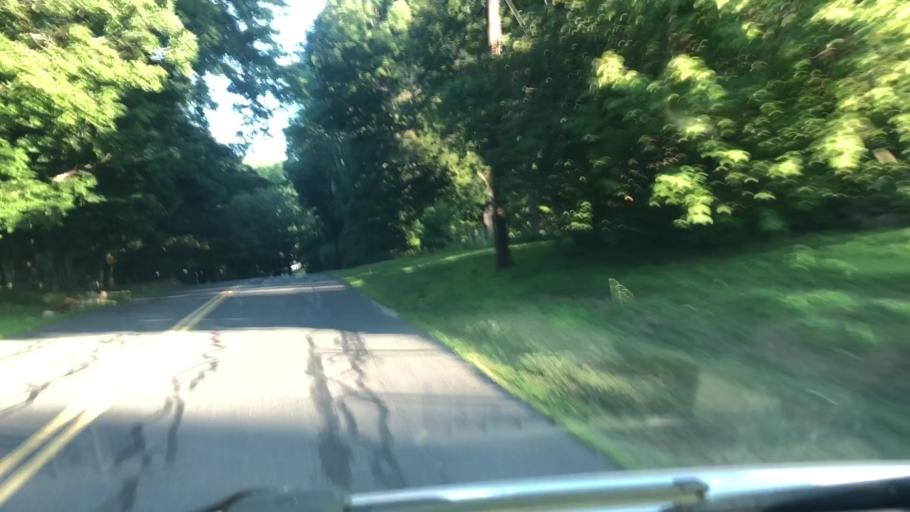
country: US
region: Massachusetts
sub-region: Hampshire County
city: Williamsburg
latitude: 42.3691
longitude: -72.7286
